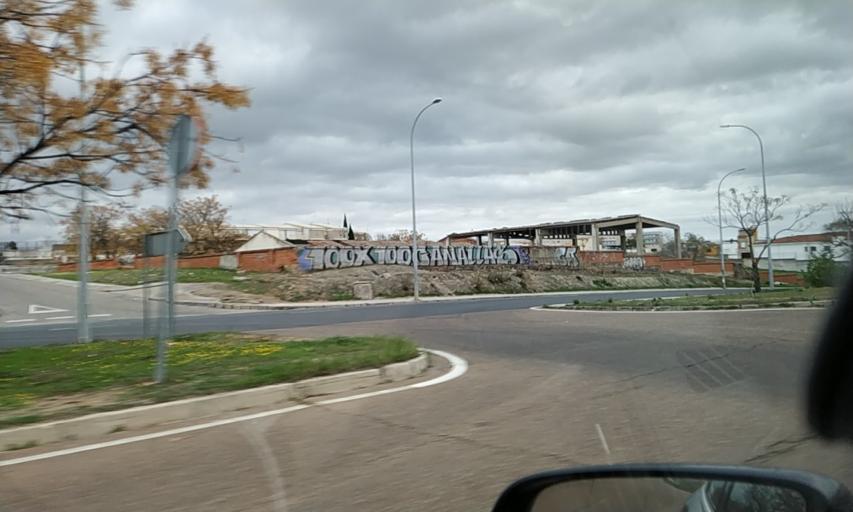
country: ES
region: Extremadura
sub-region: Provincia de Badajoz
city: Badajoz
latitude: 38.8955
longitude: -6.9839
